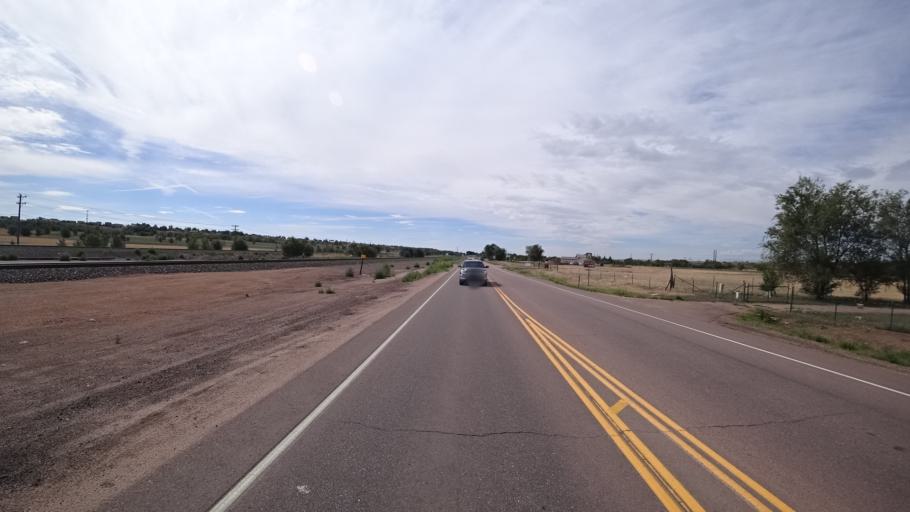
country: US
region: Colorado
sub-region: El Paso County
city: Security-Widefield
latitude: 38.7150
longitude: -104.7143
